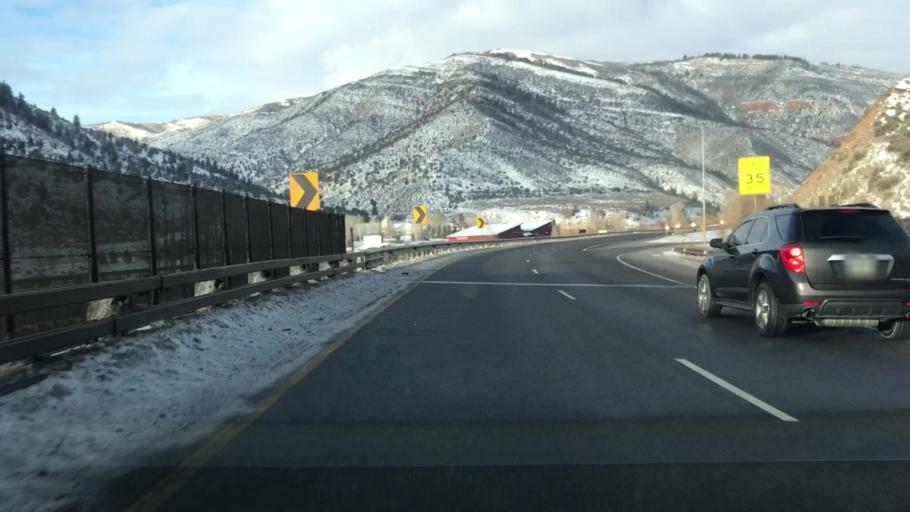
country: US
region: Colorado
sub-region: Eagle County
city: Edwards
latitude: 39.6540
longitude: -106.6344
